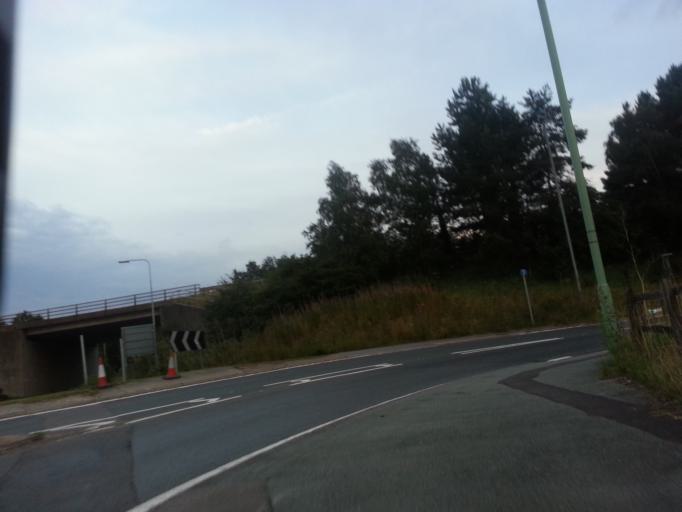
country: GB
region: England
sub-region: Suffolk
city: Kesgrave
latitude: 52.0259
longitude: 1.2074
